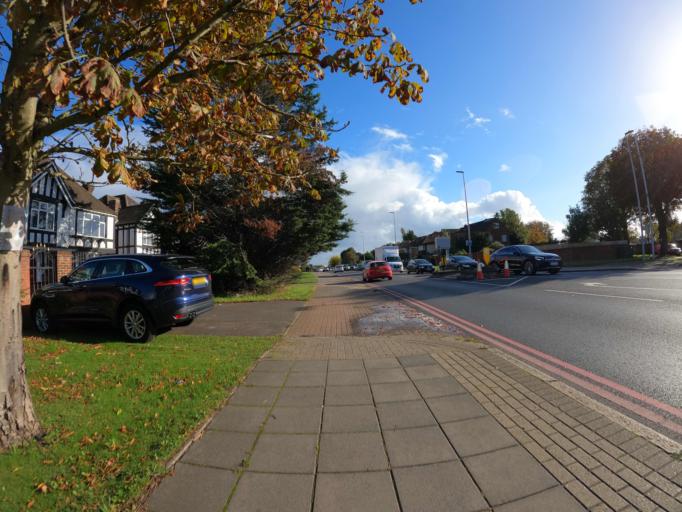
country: GB
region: England
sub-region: Greater London
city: Acton
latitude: 51.5030
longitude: -0.2884
